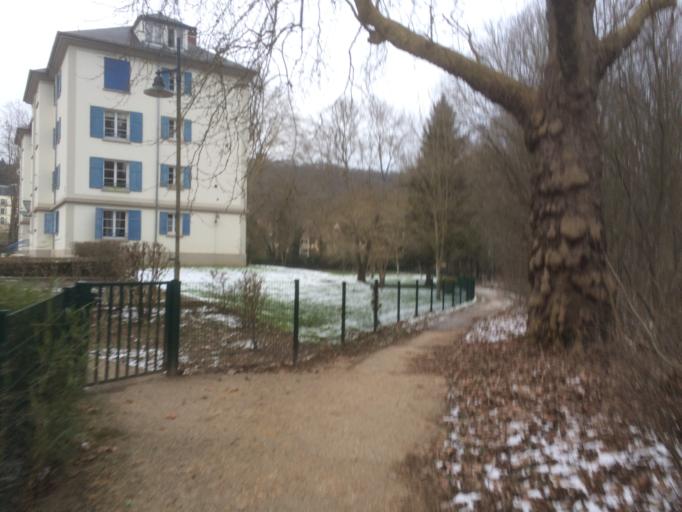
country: FR
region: Ile-de-France
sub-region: Departement de l'Essonne
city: Gif-sur-Yvette
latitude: 48.6997
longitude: 2.1368
